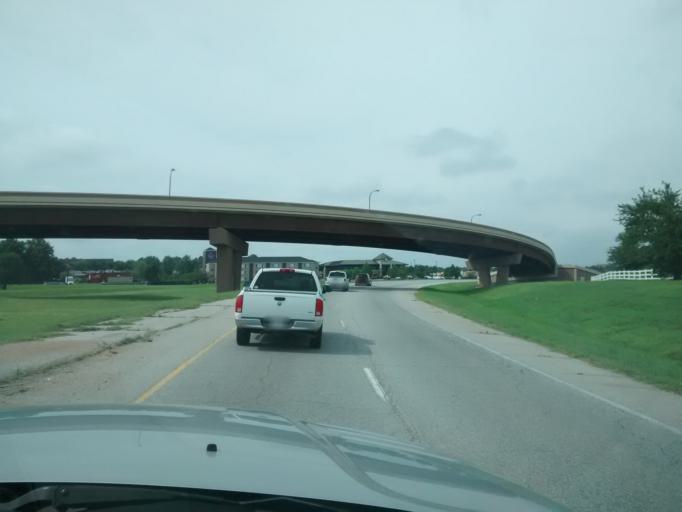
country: US
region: Arkansas
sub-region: Washington County
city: Johnson
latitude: 36.1185
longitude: -94.1459
